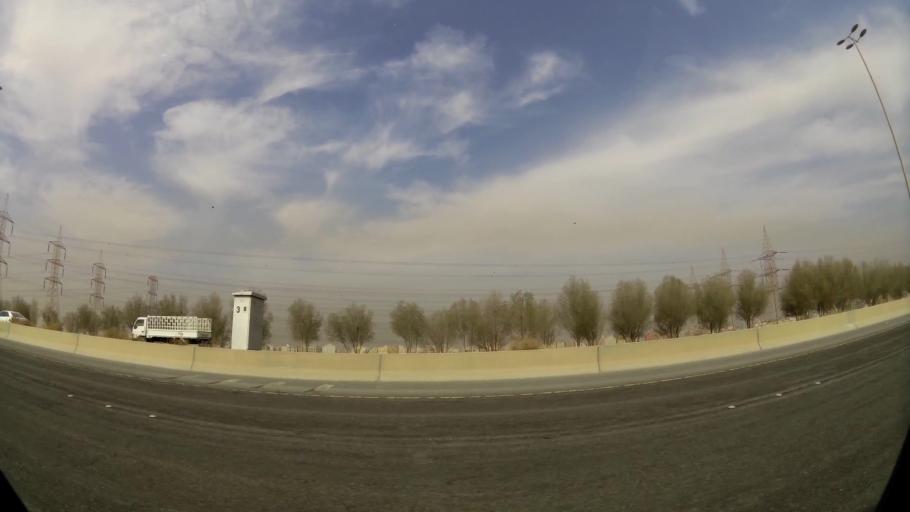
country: KW
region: Muhafazat al Jahra'
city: Al Jahra'
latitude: 29.3272
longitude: 47.7872
